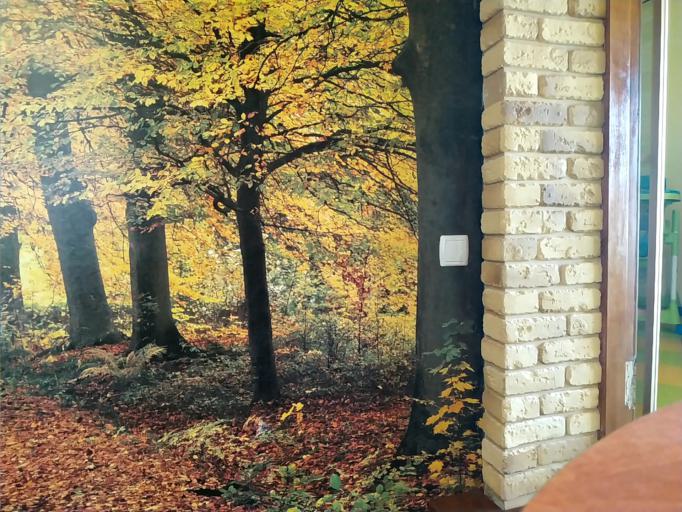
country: RU
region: Tverskaya
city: Maksatikha
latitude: 57.5908
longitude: 35.9331
